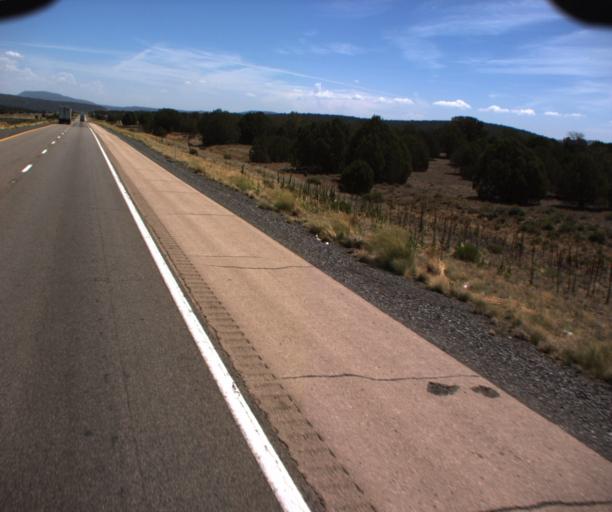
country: US
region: Arizona
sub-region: Mohave County
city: Peach Springs
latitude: 35.2140
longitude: -113.2576
